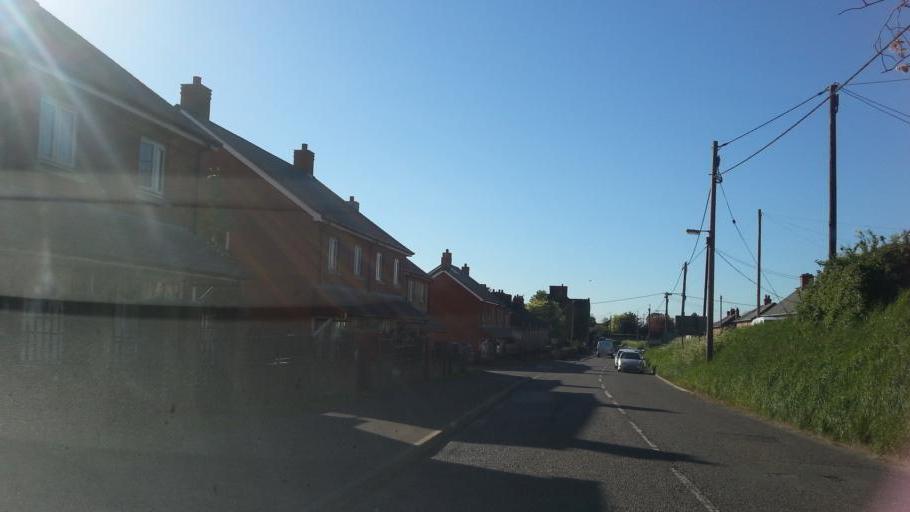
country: GB
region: England
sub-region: Somerset
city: Castle Cary
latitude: 51.0912
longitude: -2.5085
